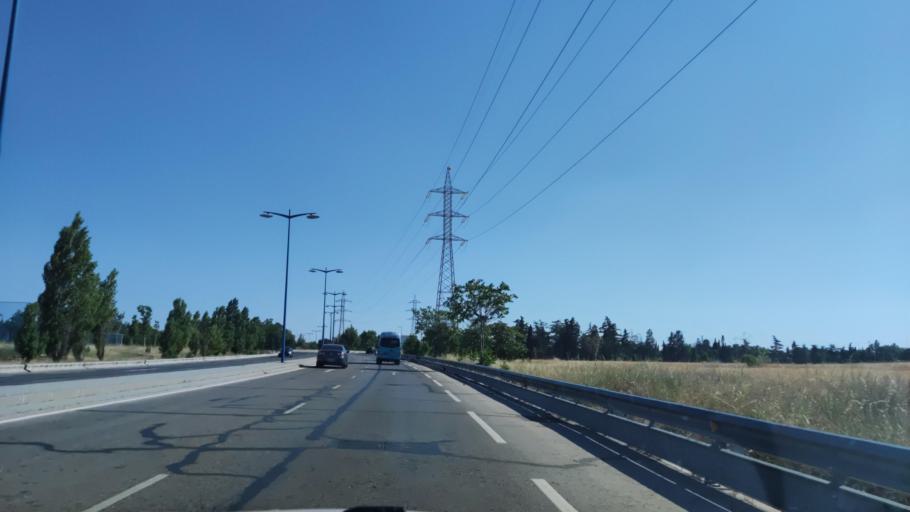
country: ES
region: Madrid
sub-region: Provincia de Madrid
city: Leganes
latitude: 40.3424
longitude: -3.7875
